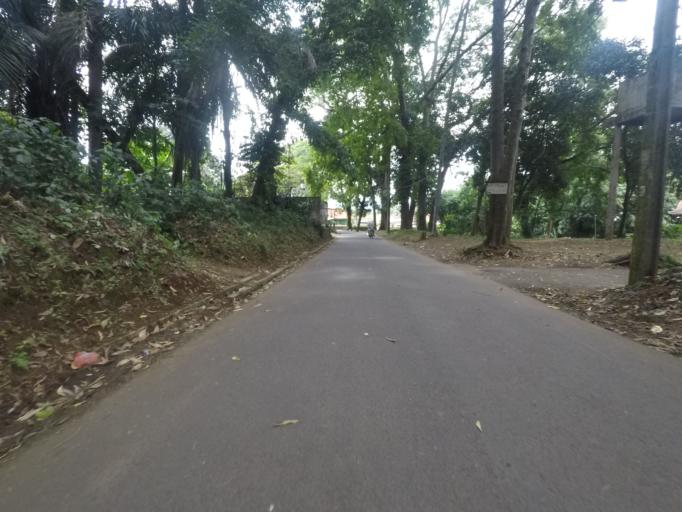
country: ID
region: West Java
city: Ciampea
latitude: -6.5497
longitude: 106.7465
